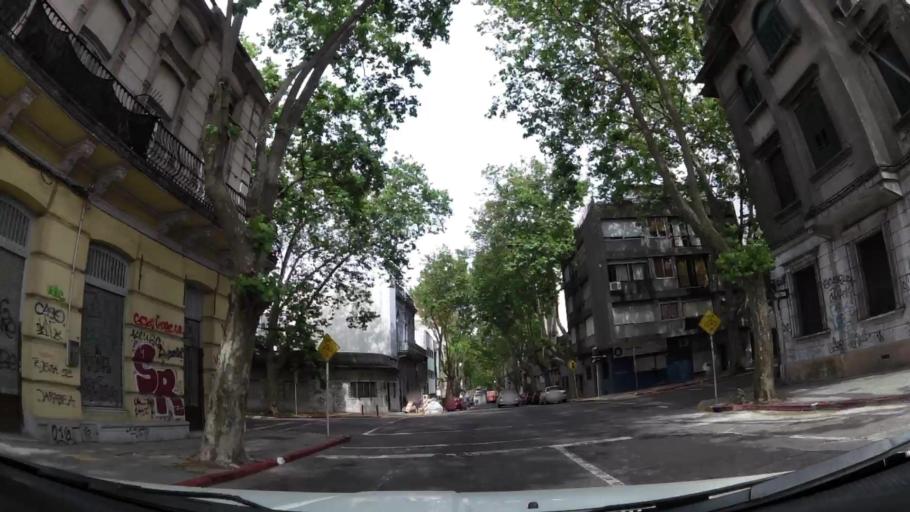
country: UY
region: Montevideo
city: Montevideo
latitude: -34.9081
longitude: -56.1819
